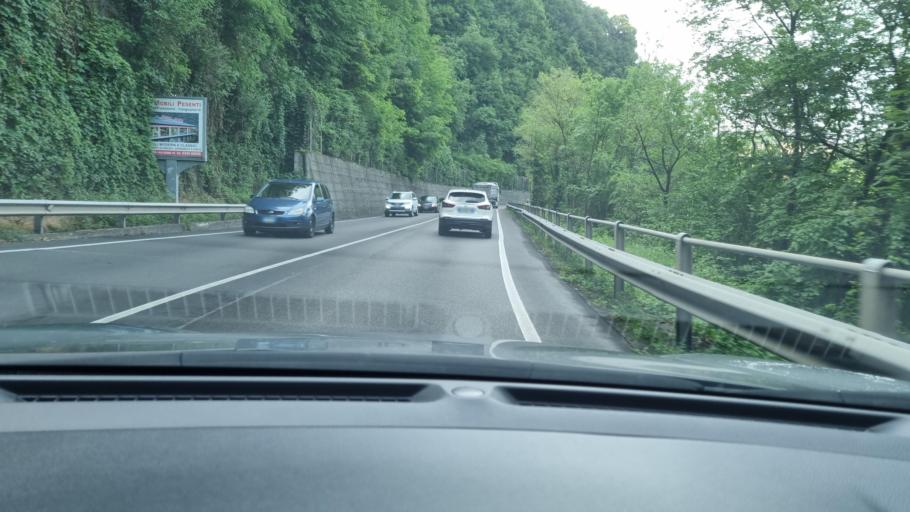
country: IT
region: Lombardy
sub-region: Provincia di Bergamo
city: Ubiale
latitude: 45.7742
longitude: 9.6149
